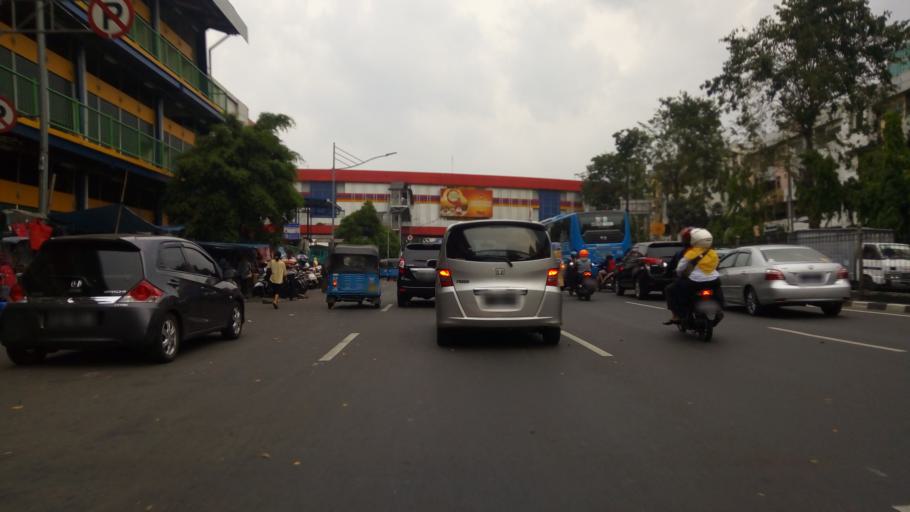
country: ID
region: Jakarta Raya
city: Jakarta
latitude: -6.1744
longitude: 106.8412
